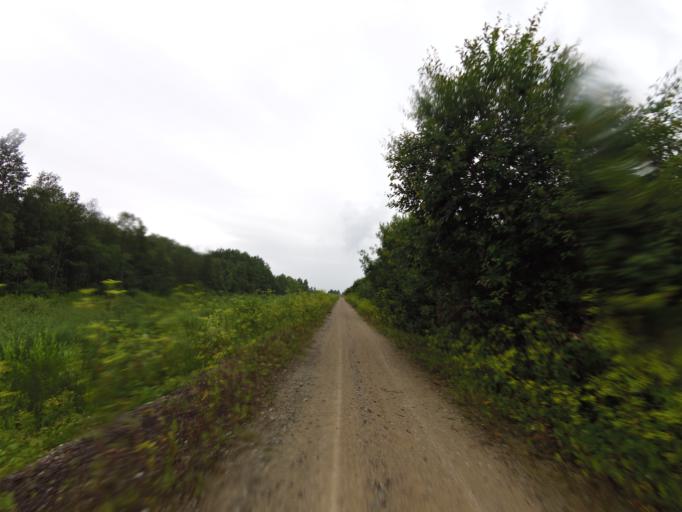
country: EE
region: Laeaene
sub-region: Ridala Parish
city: Uuemoisa
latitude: 58.9547
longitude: 23.8272
